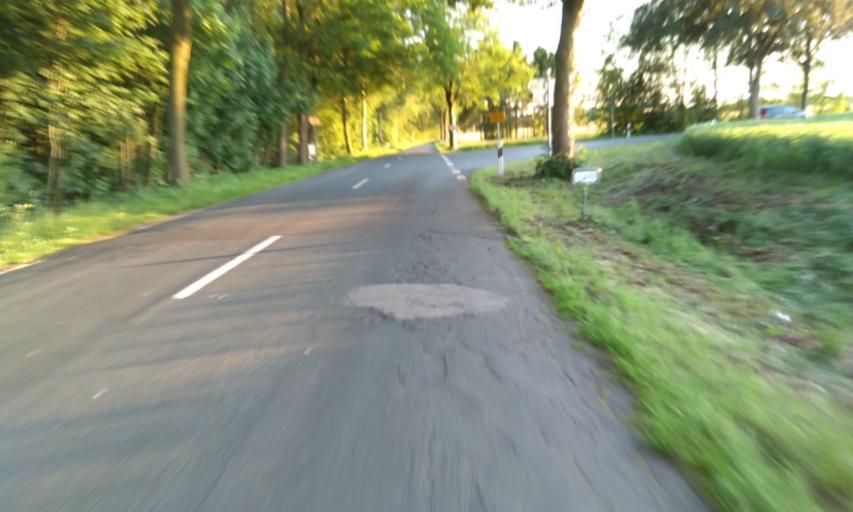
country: DE
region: Lower Saxony
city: Ahlerstedt
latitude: 53.4267
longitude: 9.4482
